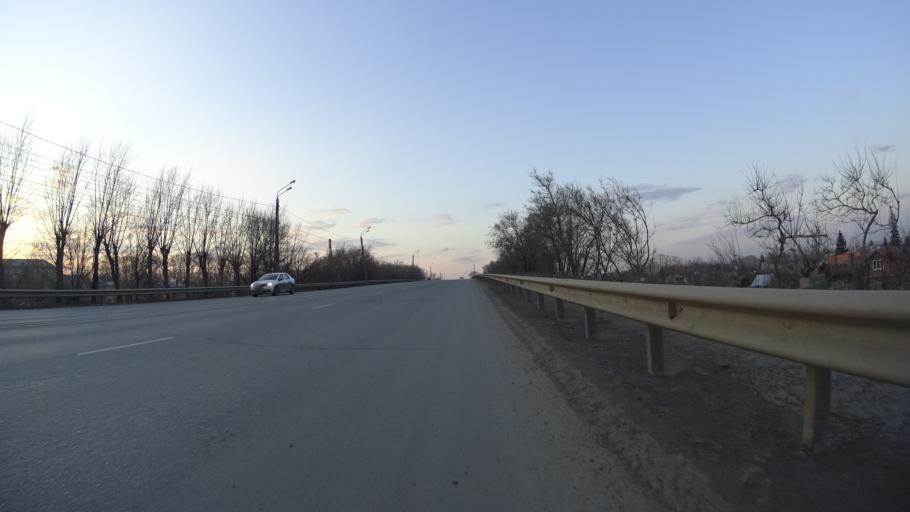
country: RU
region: Chelyabinsk
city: Novosineglazovskiy
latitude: 55.0998
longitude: 61.3878
